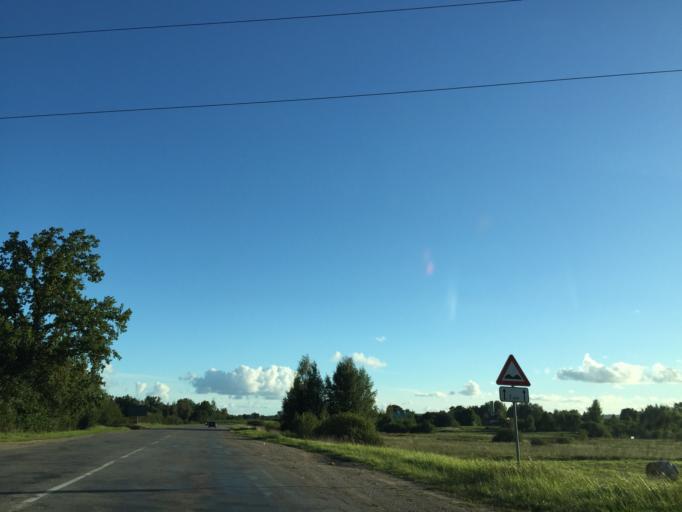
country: LV
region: Kuldigas Rajons
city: Kuldiga
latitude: 56.9696
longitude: 22.0145
